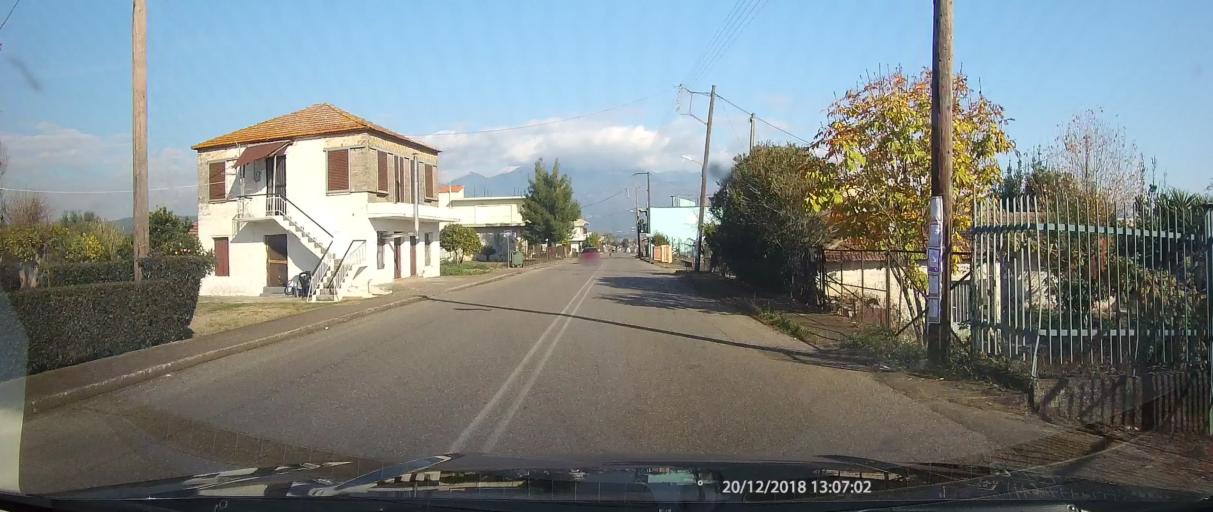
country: GR
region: West Greece
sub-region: Nomos Aitolias kai Akarnanias
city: Panaitolion
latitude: 38.5860
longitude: 21.4526
